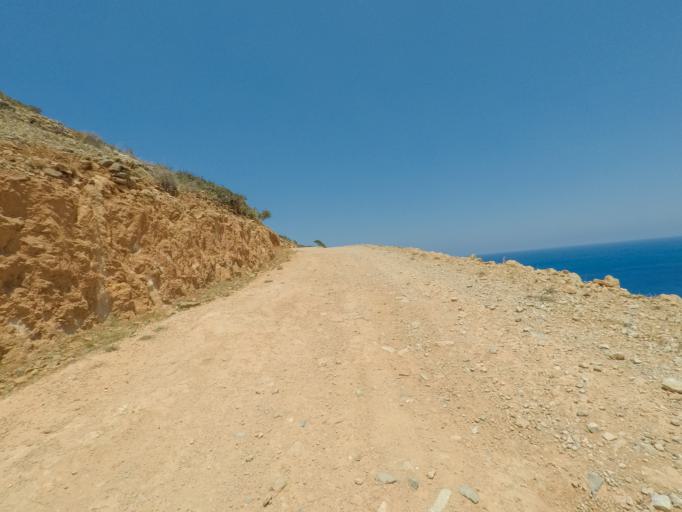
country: GR
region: Crete
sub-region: Nomos Lasithiou
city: Elounda
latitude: 35.3145
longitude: 25.7498
